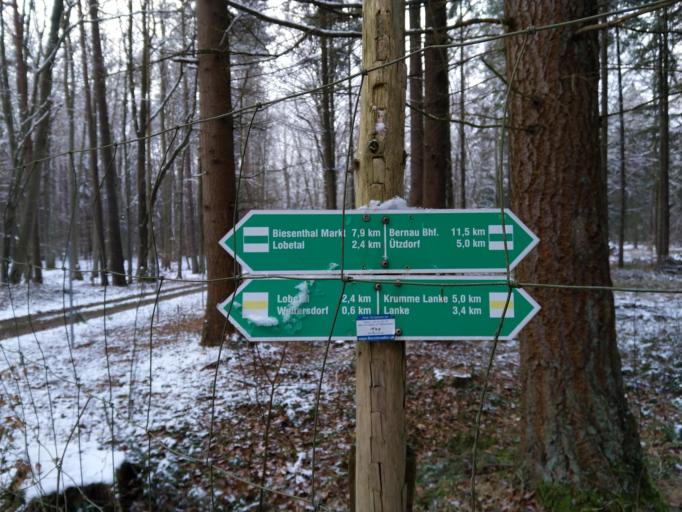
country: DE
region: Brandenburg
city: Bernau bei Berlin
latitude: 52.7349
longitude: 13.5626
